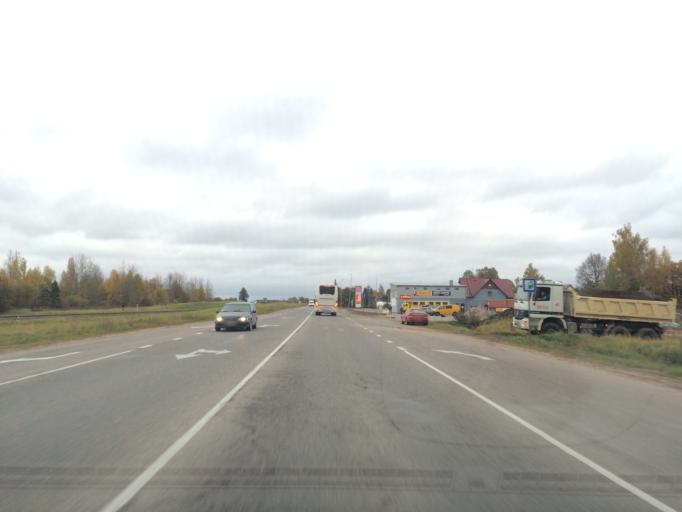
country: LV
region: Jekabpils Rajons
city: Jekabpils
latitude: 56.5114
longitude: 25.8728
